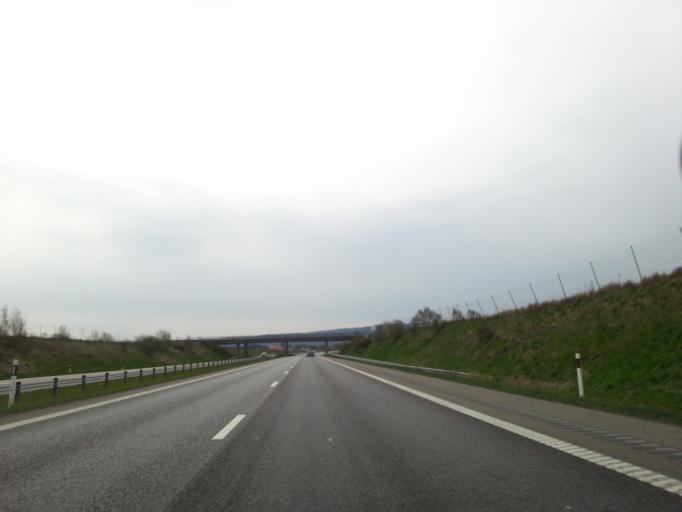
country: SE
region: Halland
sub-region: Laholms Kommun
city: Mellbystrand
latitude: 56.4504
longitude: 12.9501
